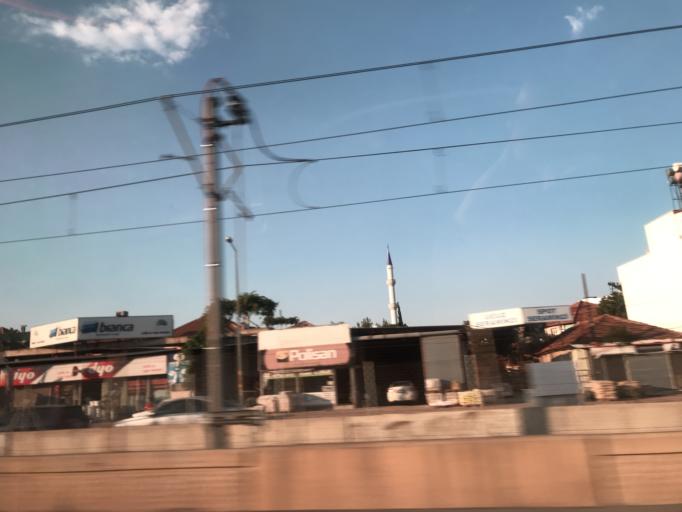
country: TR
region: Antalya
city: Antalya
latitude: 36.9353
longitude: 30.6559
